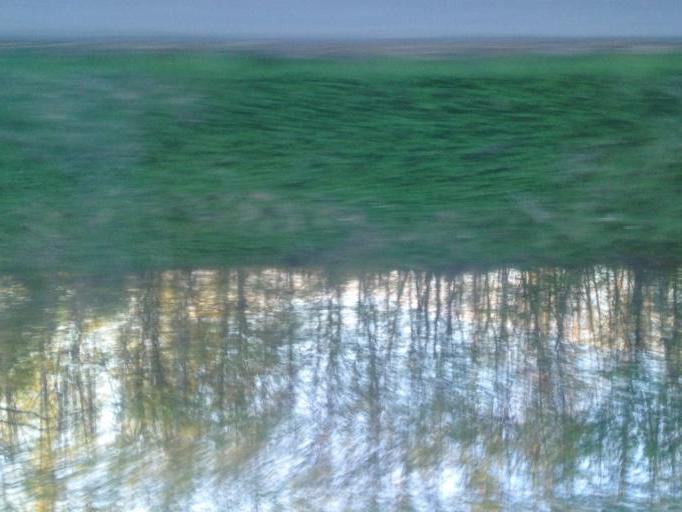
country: FI
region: Haeme
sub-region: Haemeenlinna
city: Janakkala
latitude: 60.8659
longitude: 24.5817
